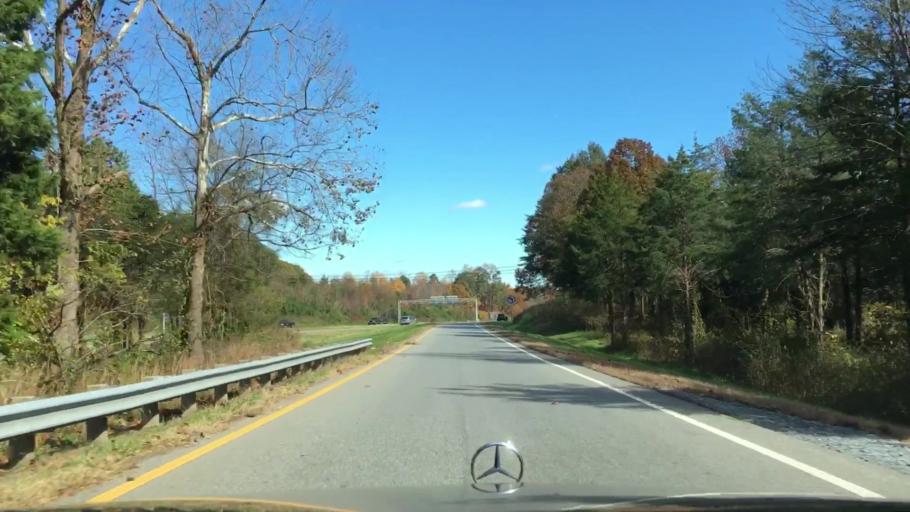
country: US
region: Virginia
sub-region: Campbell County
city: Altavista
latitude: 37.1281
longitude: -79.3054
